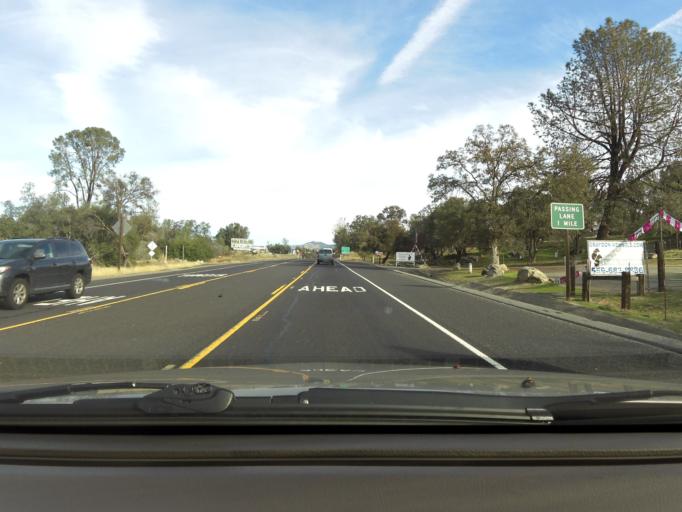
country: US
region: California
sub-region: Madera County
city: Coarsegold
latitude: 37.2158
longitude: -119.7080
